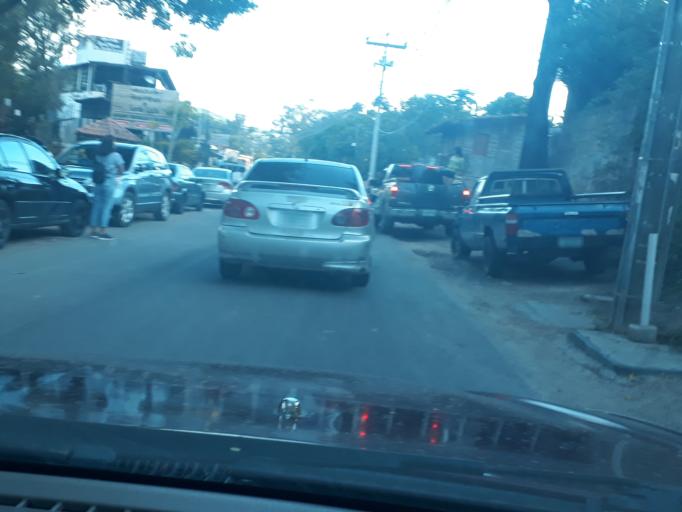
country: HN
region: Francisco Morazan
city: El Chimbo
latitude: 14.1186
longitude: -87.1124
